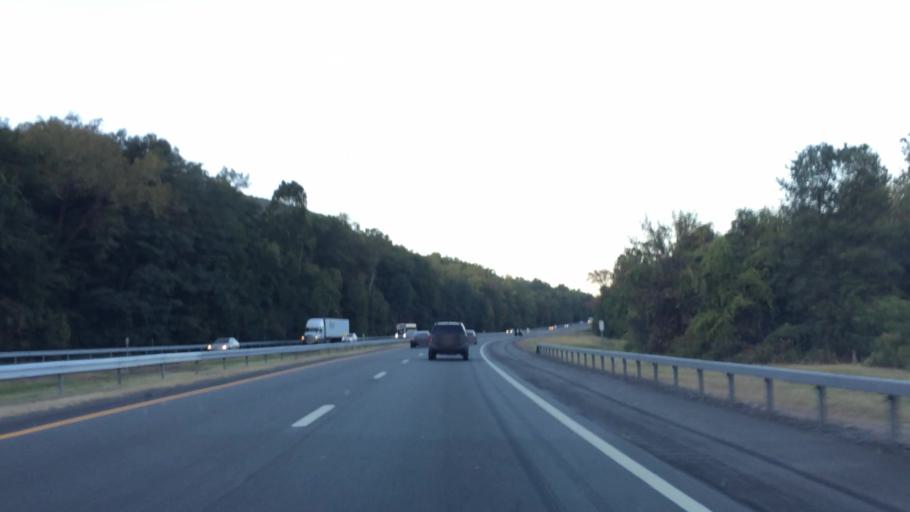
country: US
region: New York
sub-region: Orange County
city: Woodbury
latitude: 41.3803
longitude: -74.1028
